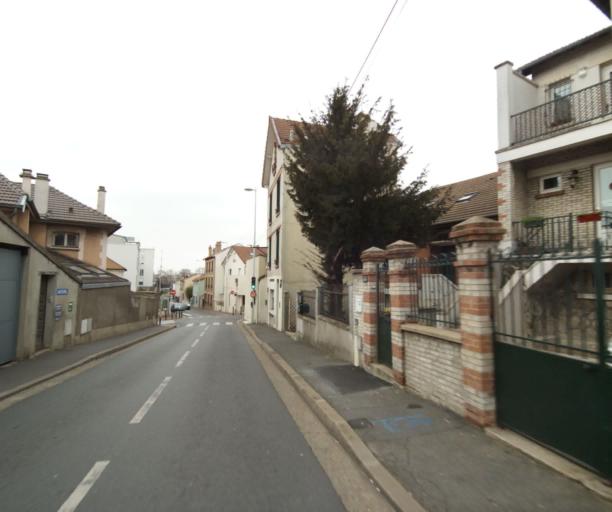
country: FR
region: Ile-de-France
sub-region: Departement des Hauts-de-Seine
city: Nanterre
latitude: 48.8854
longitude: 2.2011
